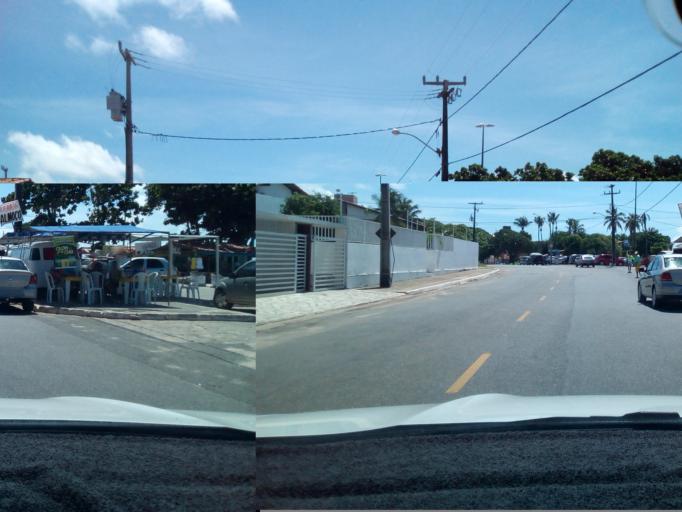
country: BR
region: Paraiba
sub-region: Joao Pessoa
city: Joao Pessoa
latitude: -7.1552
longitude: -34.7936
